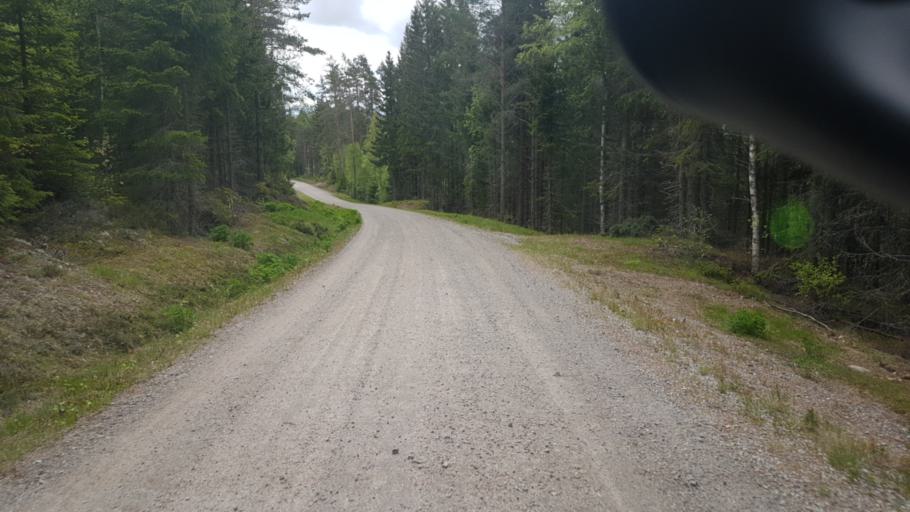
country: SE
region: Vaermland
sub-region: Arvika Kommun
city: Arvika
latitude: 59.8345
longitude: 12.8155
